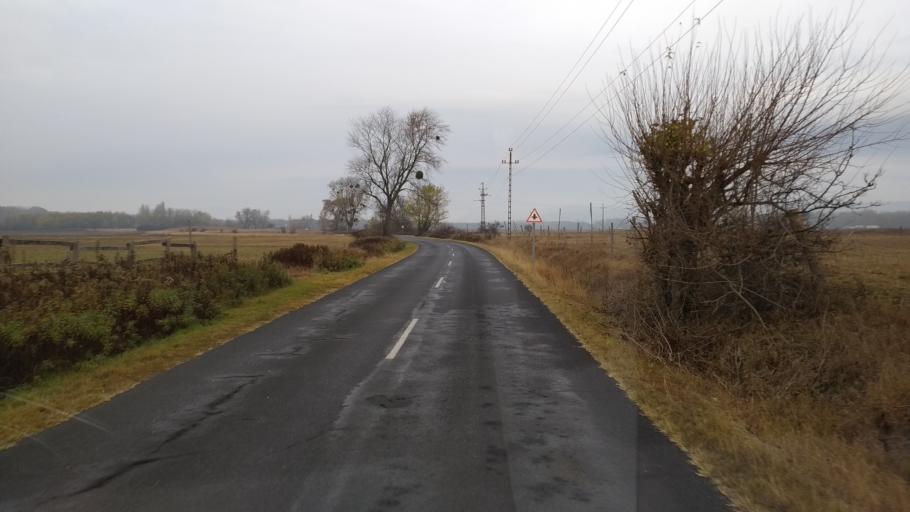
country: HU
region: Pest
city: Tahitotfalu
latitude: 47.7869
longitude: 19.0895
